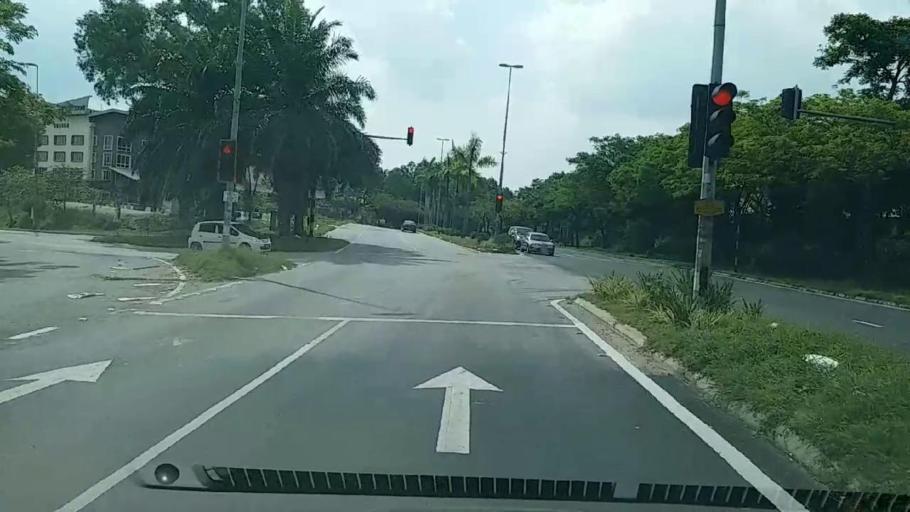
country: MY
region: Putrajaya
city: Putrajaya
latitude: 2.9651
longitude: 101.6157
